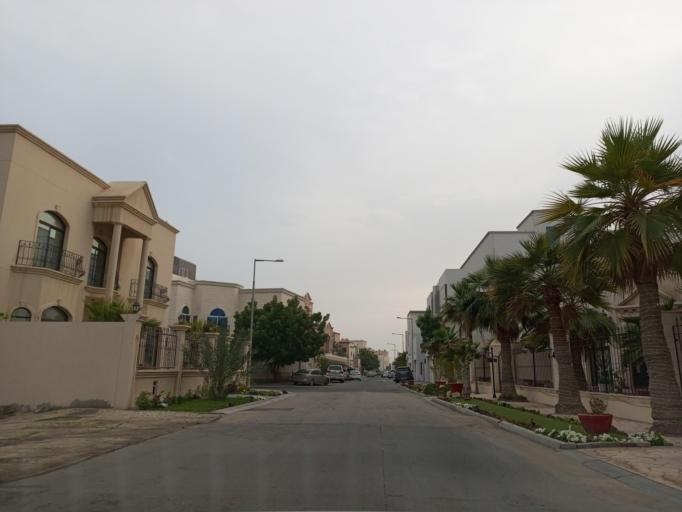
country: BH
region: Muharraq
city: Al Hadd
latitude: 26.2449
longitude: 50.6419
